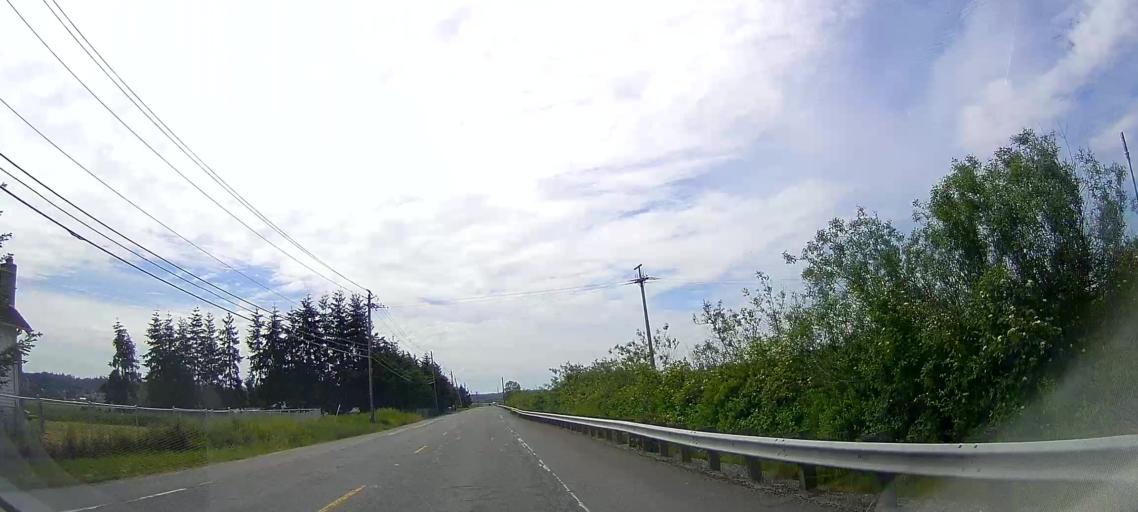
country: US
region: Washington
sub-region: Skagit County
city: Mount Vernon
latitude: 48.3500
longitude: -122.3350
